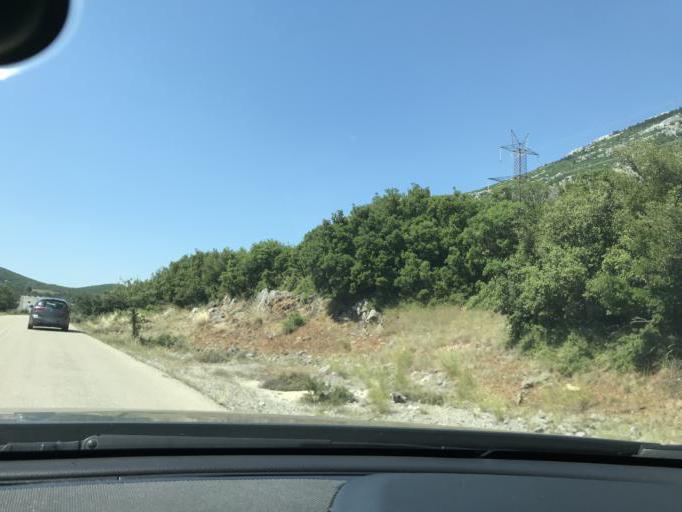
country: GR
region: Central Greece
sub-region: Nomos Voiotias
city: Distomo
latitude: 38.5084
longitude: 22.7064
